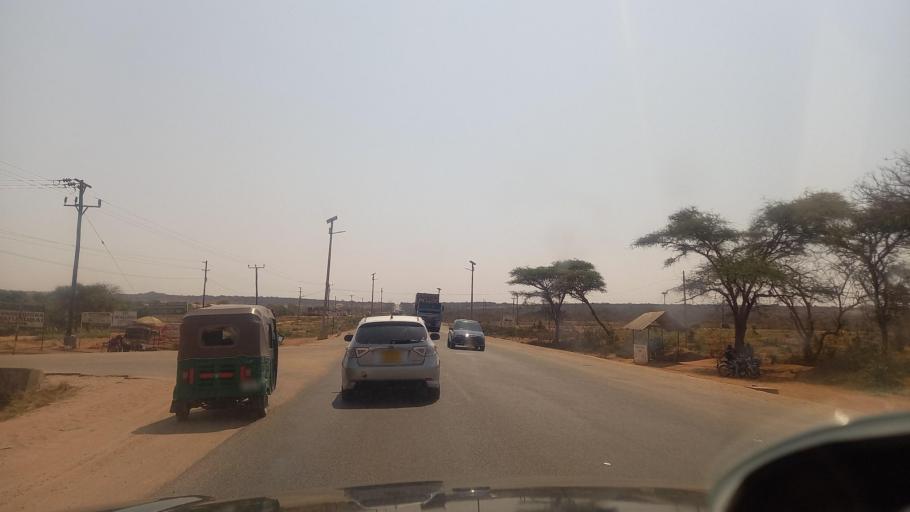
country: TZ
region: Dodoma
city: Kisasa
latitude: -6.1459
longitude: 35.8295
